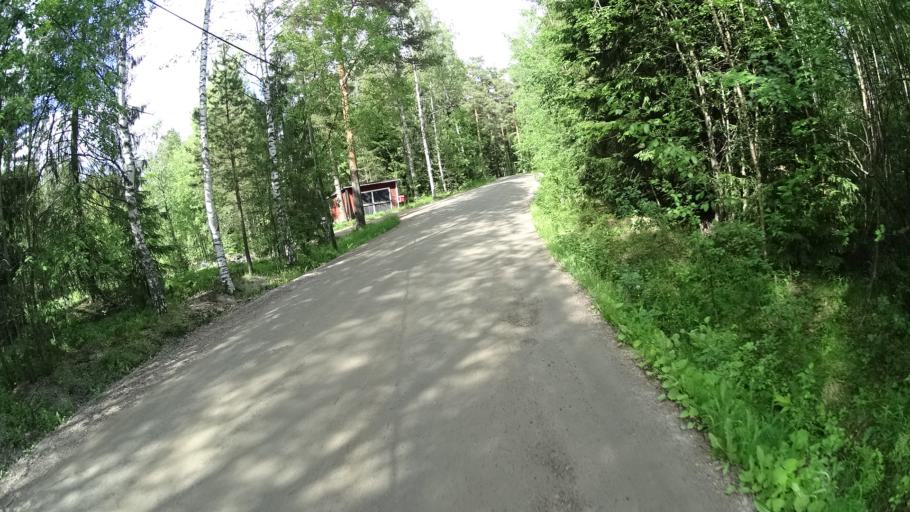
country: FI
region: Uusimaa
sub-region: Helsinki
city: Sibbo
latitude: 60.2858
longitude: 25.3118
